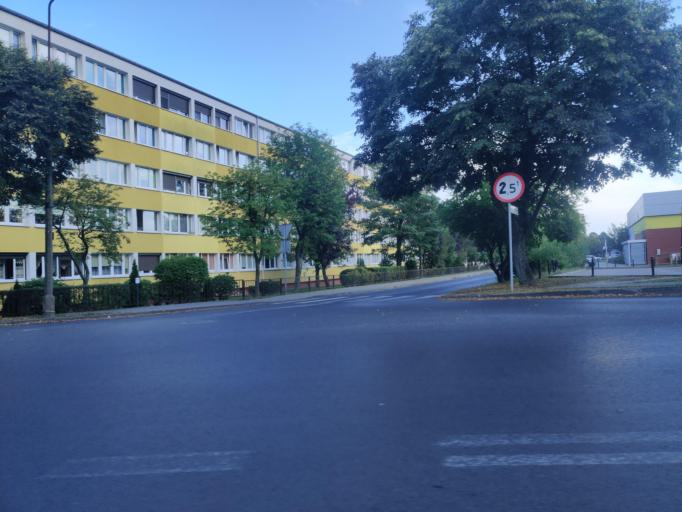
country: PL
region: Greater Poland Voivodeship
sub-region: Konin
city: Konin
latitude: 52.2299
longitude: 18.2738
